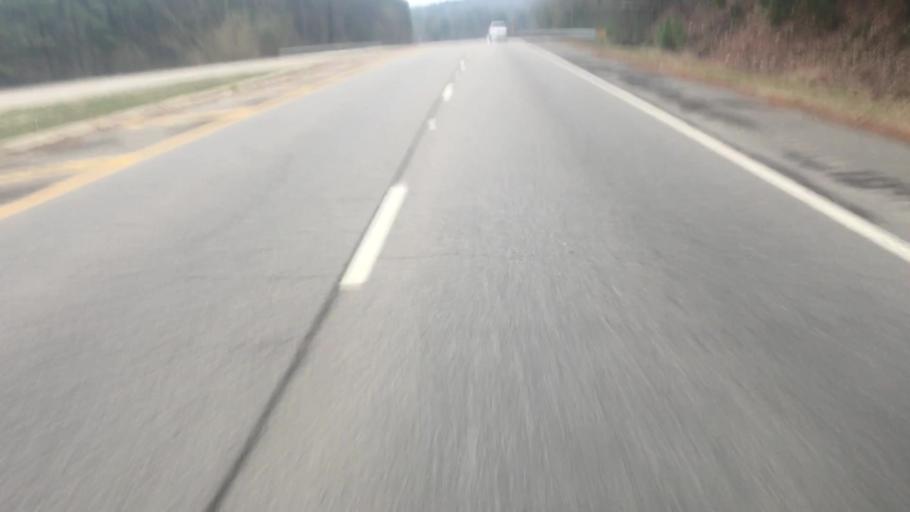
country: US
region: Alabama
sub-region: Walker County
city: Sumiton
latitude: 33.7527
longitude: -87.0603
